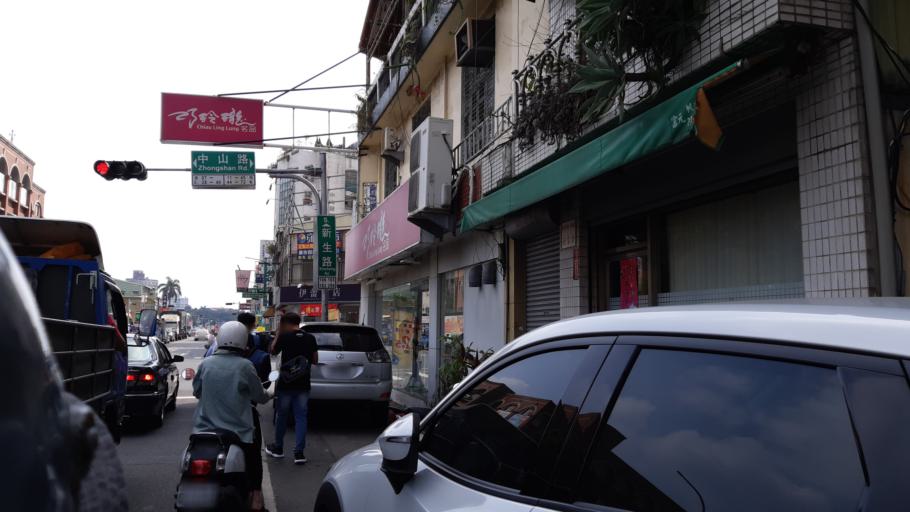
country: TW
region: Taiwan
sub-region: Chiayi
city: Jiayi Shi
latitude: 23.4828
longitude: 120.4610
